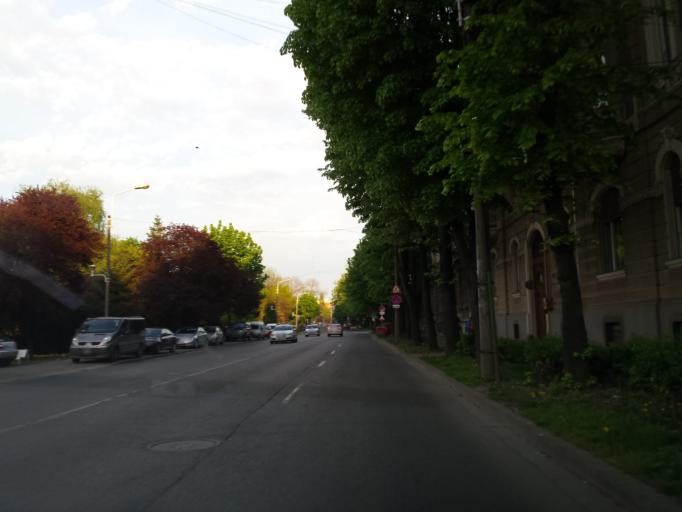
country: RO
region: Timis
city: Timisoara
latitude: 45.7487
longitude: 21.2218
